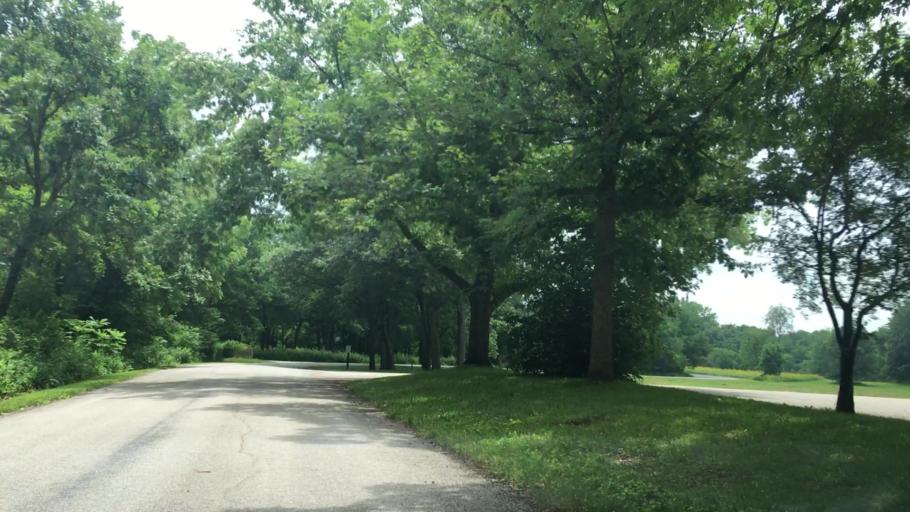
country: US
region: Iowa
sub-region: Johnson County
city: Tiffin
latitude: 41.7364
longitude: -91.7241
